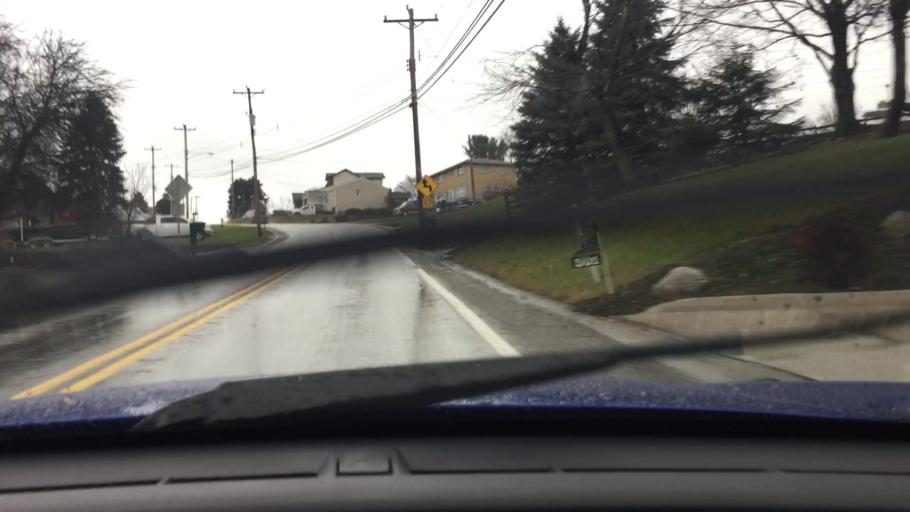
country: US
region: Pennsylvania
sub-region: Allegheny County
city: Jefferson Hills
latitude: 40.3020
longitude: -79.9193
